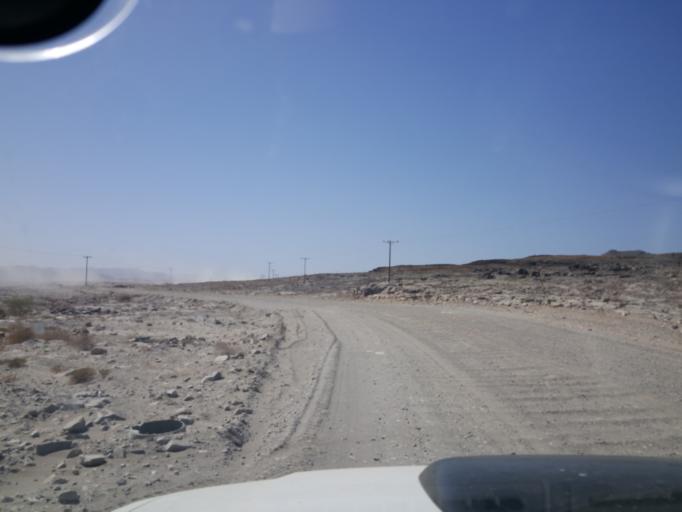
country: ZA
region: Northern Cape
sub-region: Namakwa District Municipality
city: Port Nolloth
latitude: -28.7140
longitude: 17.6000
